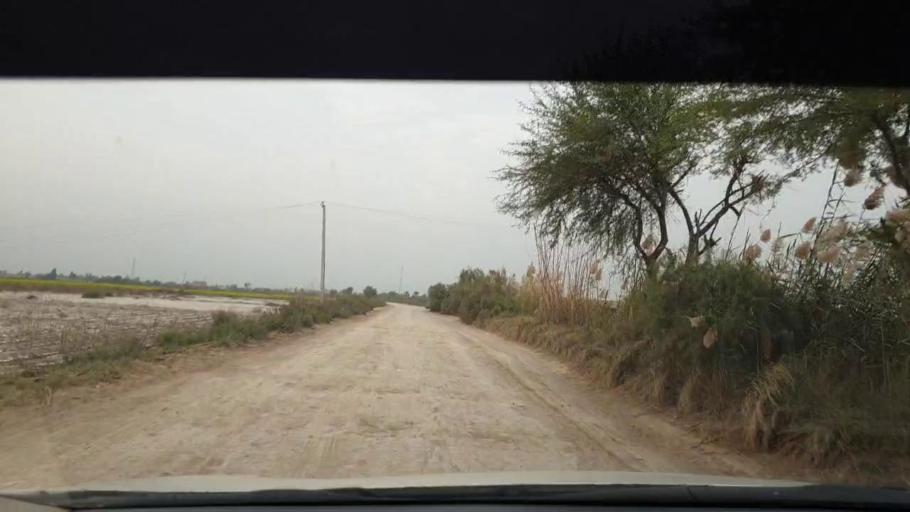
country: PK
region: Sindh
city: Sinjhoro
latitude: 25.9267
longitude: 68.7544
